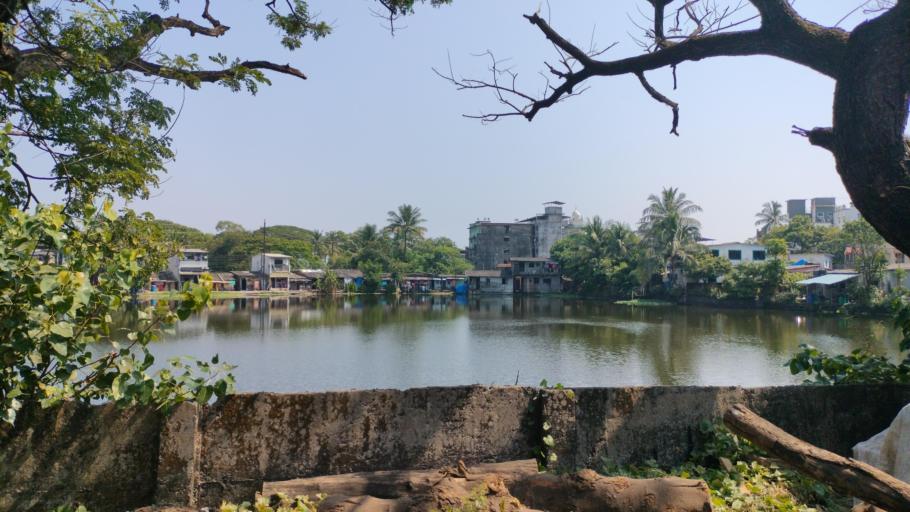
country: IN
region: Maharashtra
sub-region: Thane
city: Bhayandar
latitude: 19.3547
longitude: 72.8140
